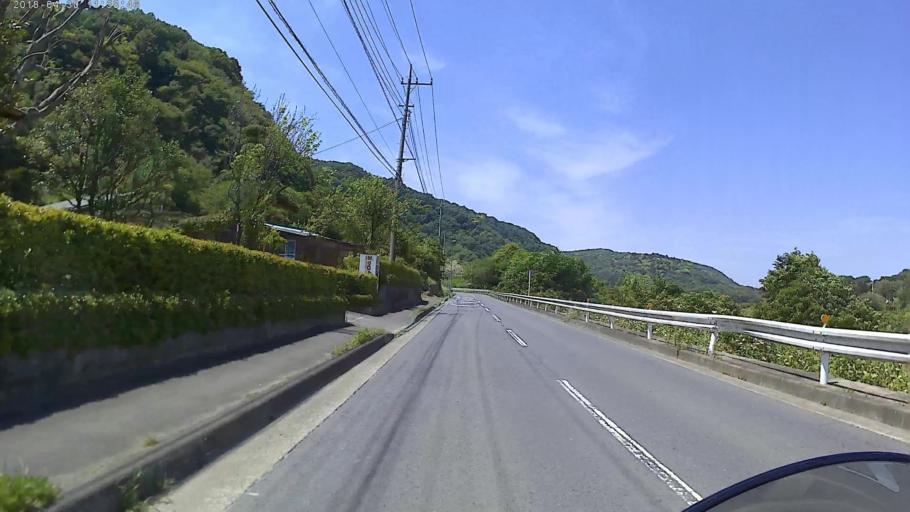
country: JP
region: Kanagawa
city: Zama
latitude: 35.5034
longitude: 139.3336
